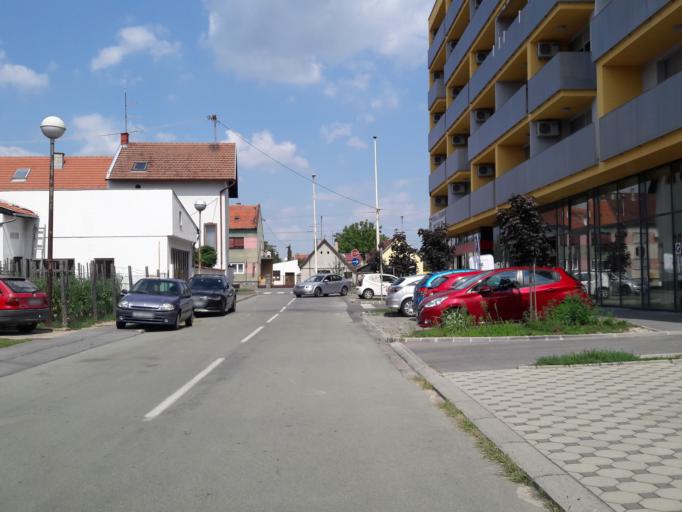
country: HR
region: Osjecko-Baranjska
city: Visnjevac
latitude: 45.5642
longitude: 18.6414
